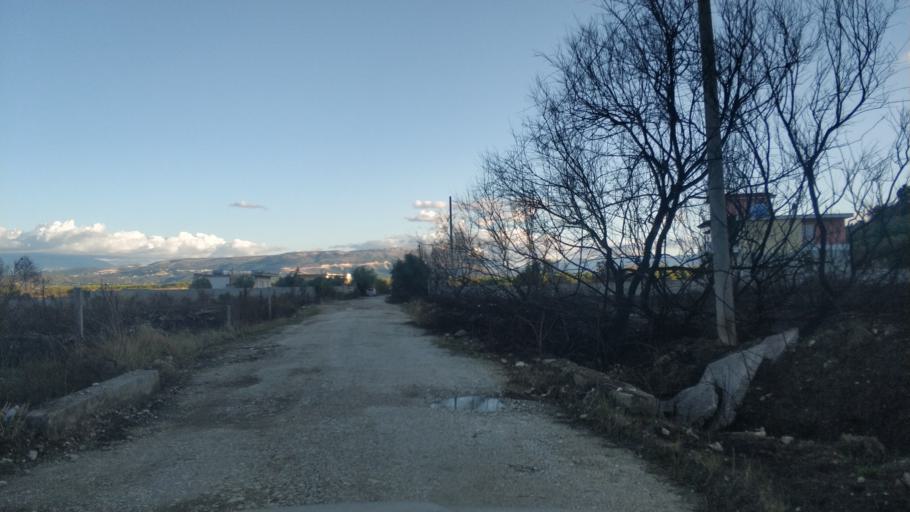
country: AL
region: Vlore
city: Vlore
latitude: 40.5101
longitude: 19.4217
